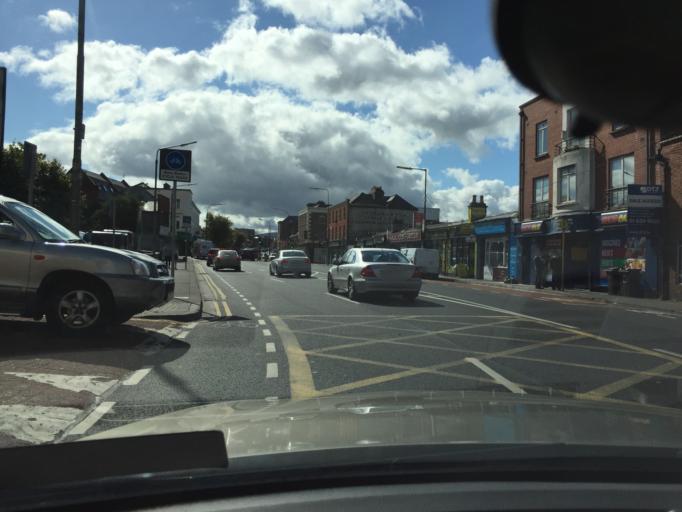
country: IE
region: Leinster
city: Rathmines
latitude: 53.3331
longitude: -6.2752
